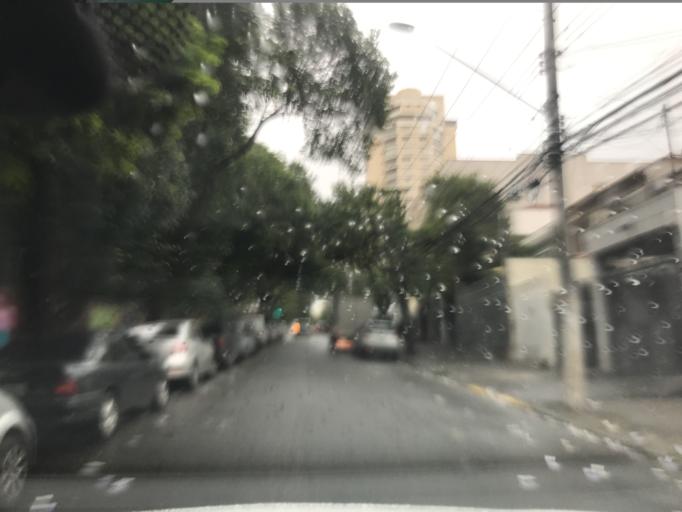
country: BR
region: Sao Paulo
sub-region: Sao Paulo
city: Sao Paulo
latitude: -23.5297
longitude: -46.6805
